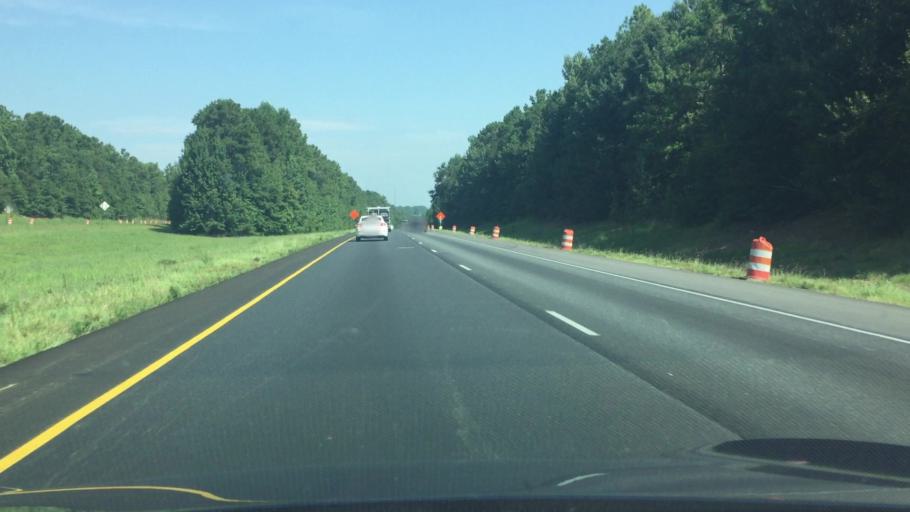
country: US
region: Alabama
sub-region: Chilton County
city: Clanton
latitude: 32.7692
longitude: -86.5649
